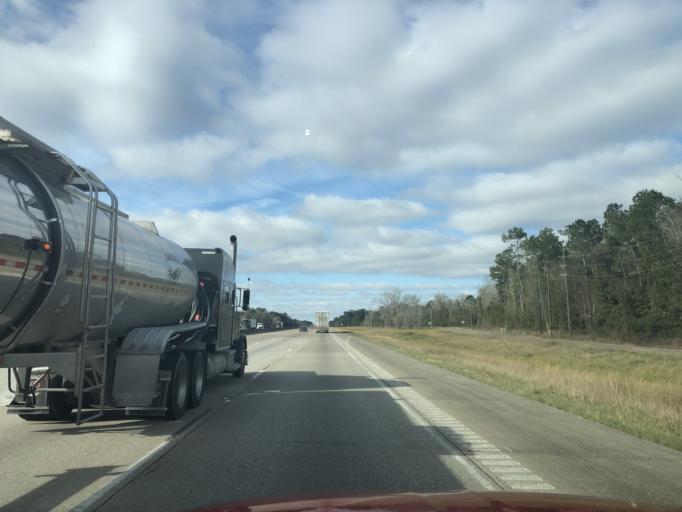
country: US
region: Texas
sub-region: Chambers County
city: Anahuac
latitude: 29.8387
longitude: -94.6070
